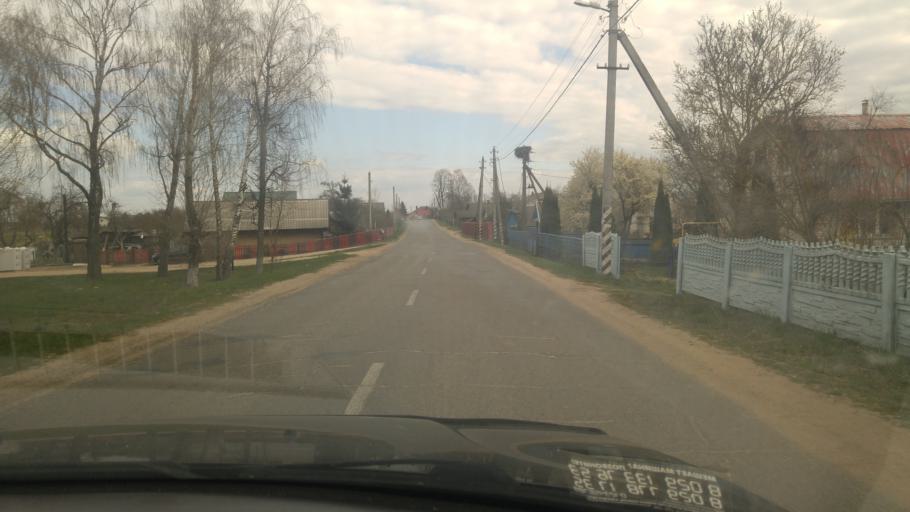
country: BY
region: Minsk
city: Rudzyensk
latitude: 53.6590
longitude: 27.7835
